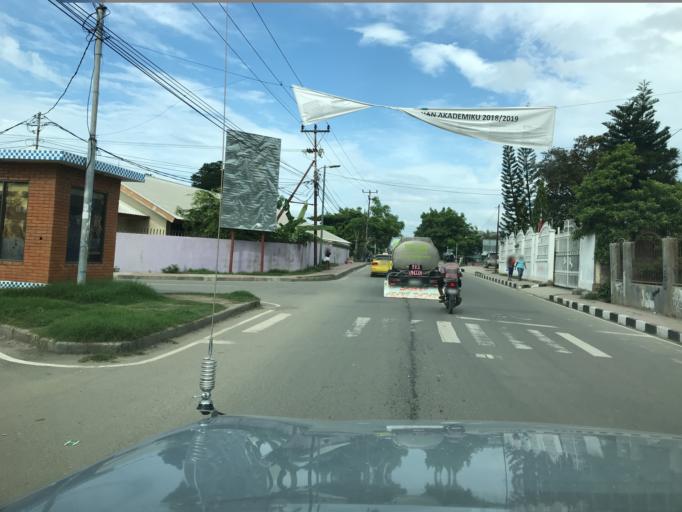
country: TL
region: Dili
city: Dili
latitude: -8.5596
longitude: 125.5640
